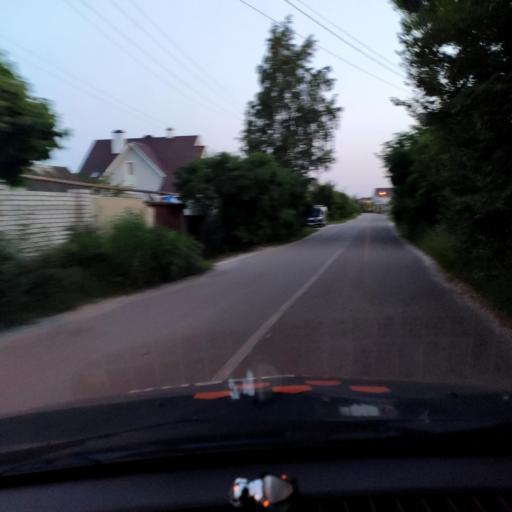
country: RU
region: Voronezj
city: Ramon'
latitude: 51.8187
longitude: 39.2671
